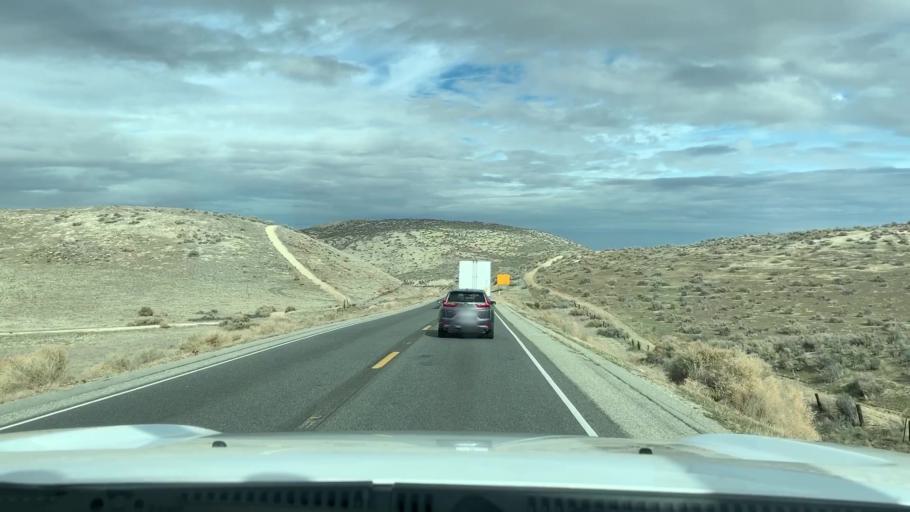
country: US
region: California
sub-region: Kern County
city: Maricopa
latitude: 34.9795
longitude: -119.4352
